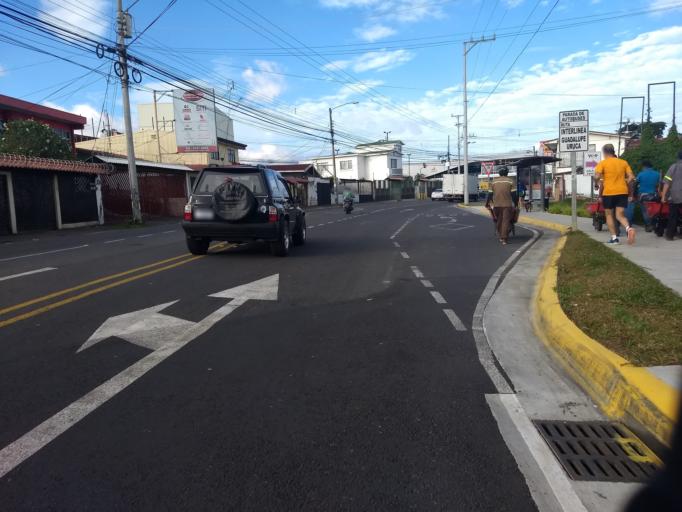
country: CR
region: San Jose
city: Colima
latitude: 9.9536
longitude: -84.0804
